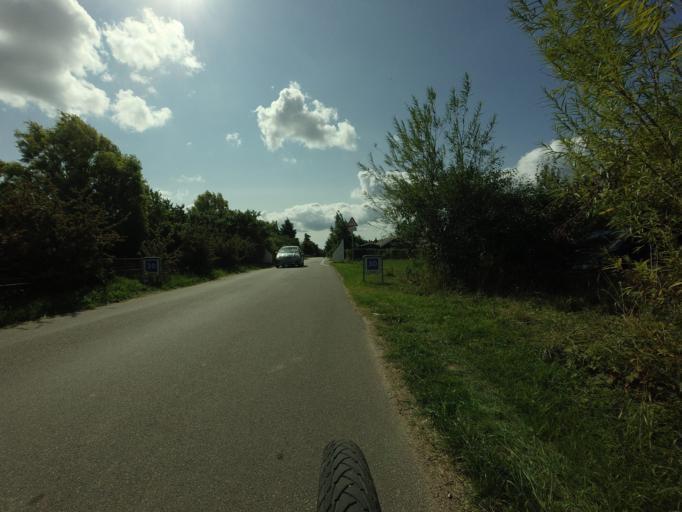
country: DK
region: Zealand
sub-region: Vordingborg Kommune
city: Stege
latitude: 54.9721
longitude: 12.3867
